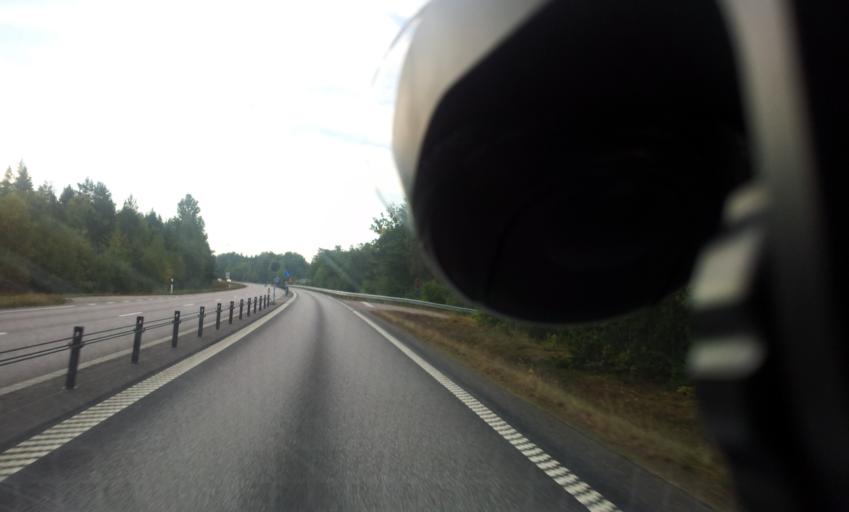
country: SE
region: Kalmar
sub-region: Oskarshamns Kommun
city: Paskallavik
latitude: 57.1316
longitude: 16.4755
